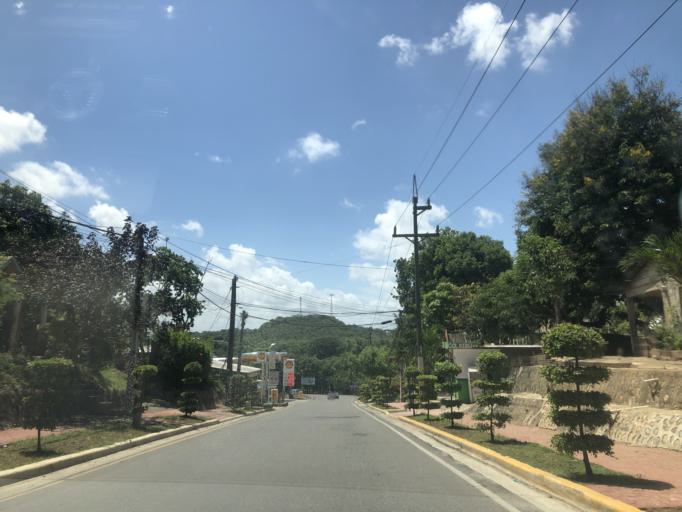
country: DO
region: Santiago
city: La Canela
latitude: 19.4517
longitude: -70.7681
